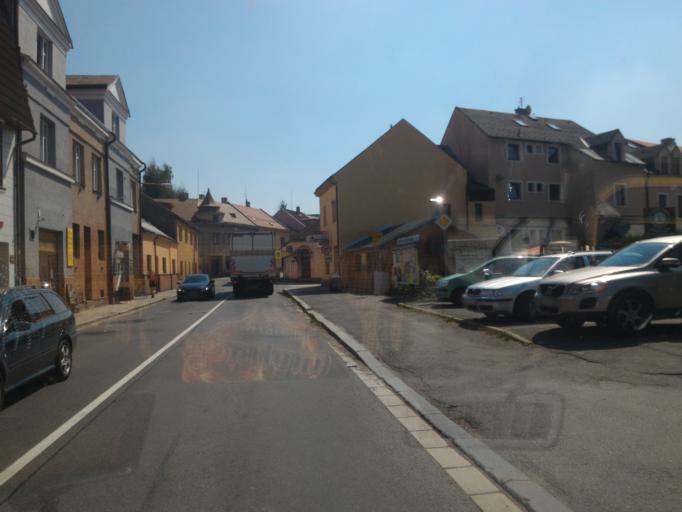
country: CZ
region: Pardubicky
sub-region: Okres Chrudim
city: Hlinsko
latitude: 49.7633
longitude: 15.9072
